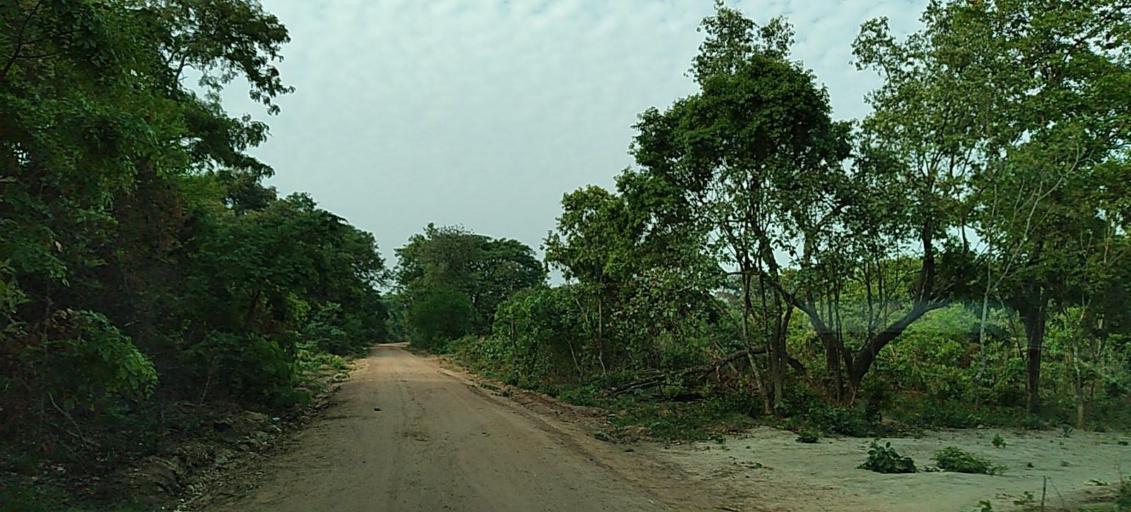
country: ZM
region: Copperbelt
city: Chingola
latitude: -12.8860
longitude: 27.6905
